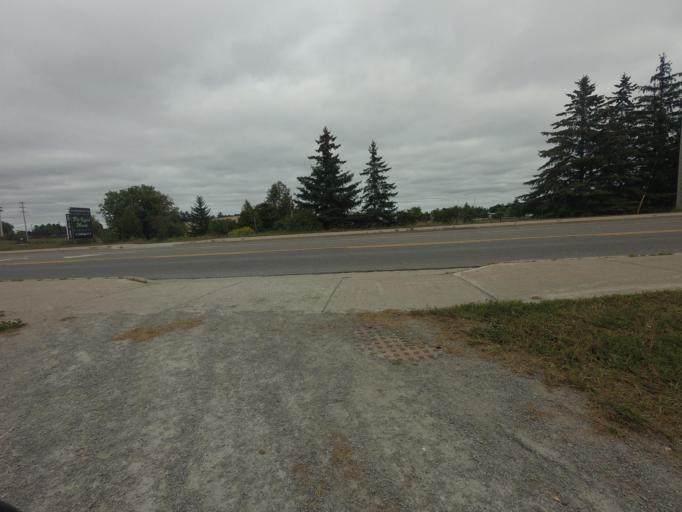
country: CA
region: Ontario
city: Omemee
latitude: 44.3402
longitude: -78.7463
